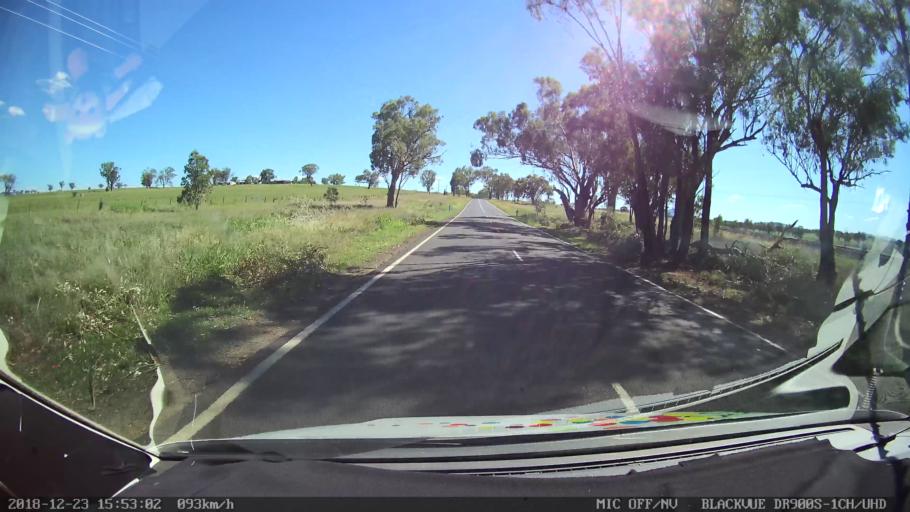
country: AU
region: New South Wales
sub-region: Tamworth Municipality
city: Phillip
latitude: -31.1284
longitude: 150.8841
